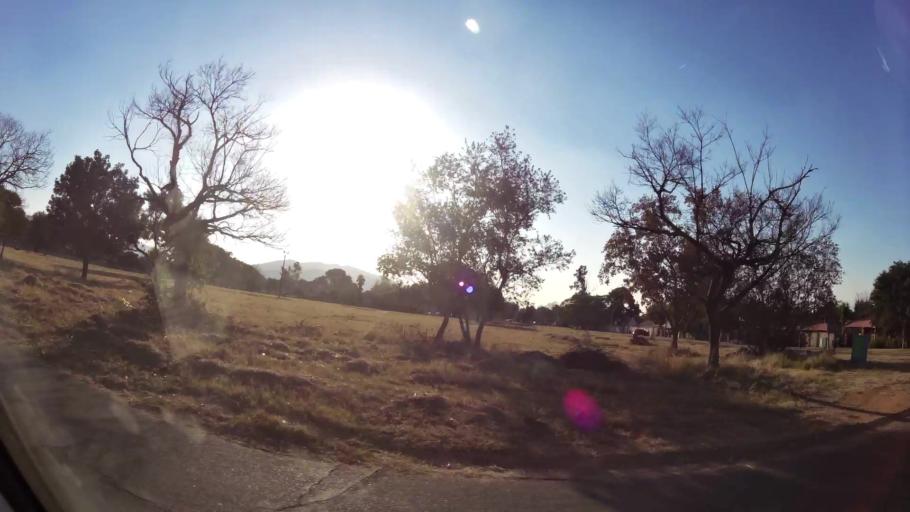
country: ZA
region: North-West
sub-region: Bojanala Platinum District Municipality
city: Rustenburg
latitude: -25.6794
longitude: 27.2287
